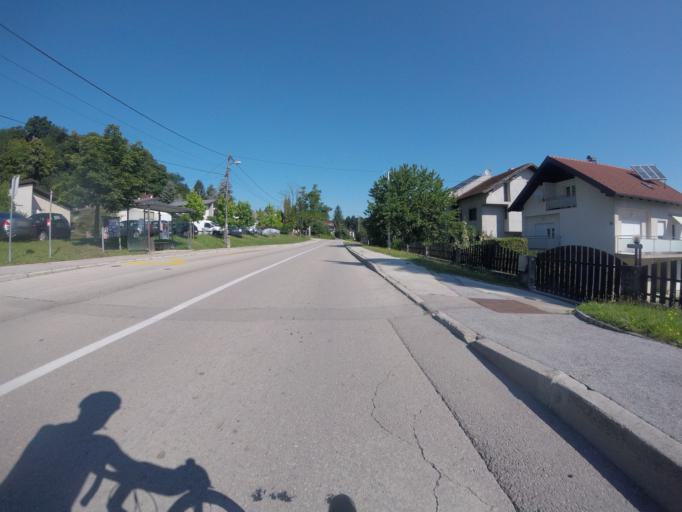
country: HR
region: Zagrebacka
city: Bregana
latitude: 45.8198
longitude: 15.7006
